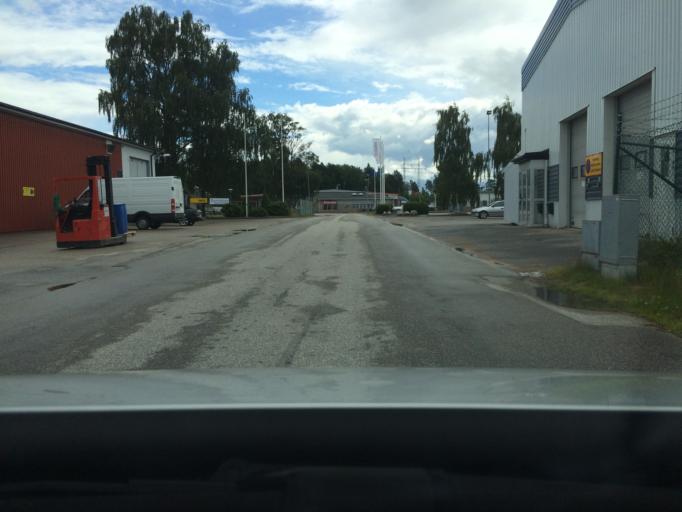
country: SE
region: Vaestra Goetaland
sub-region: Trollhattan
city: Trollhattan
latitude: 58.3015
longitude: 12.3245
